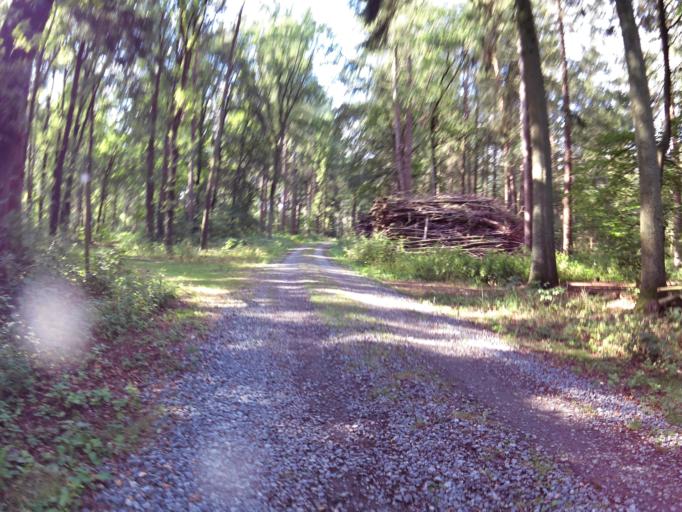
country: DE
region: Lower Saxony
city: Bremervorde
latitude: 53.4779
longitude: 9.1541
